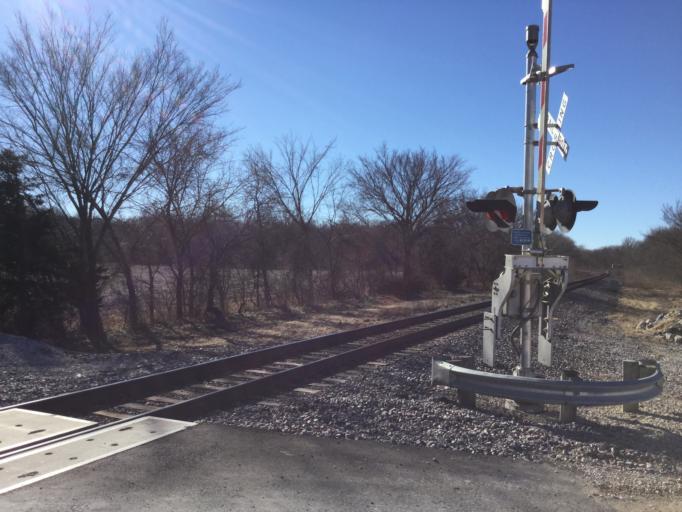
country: US
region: Kansas
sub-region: Miami County
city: Osawatomie
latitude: 38.3749
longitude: -94.9876
